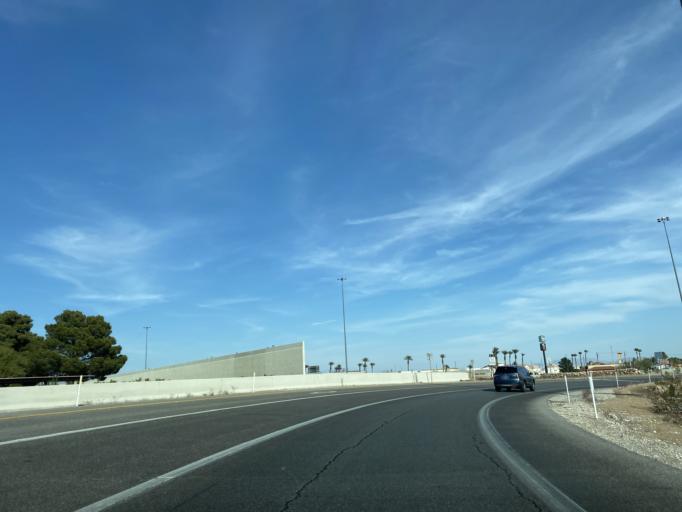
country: US
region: Nevada
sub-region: Clark County
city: Spring Valley
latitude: 36.1975
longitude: -115.2463
